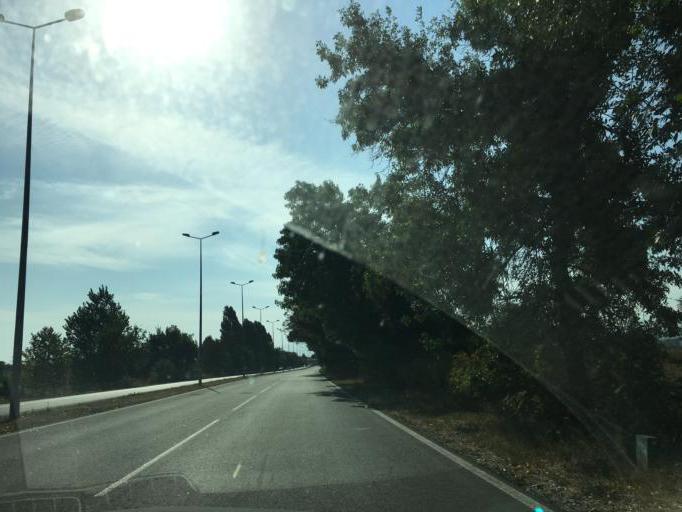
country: BG
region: Pazardzhik
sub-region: Obshtina Pazardzhik
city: Pazardzhik
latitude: 42.2173
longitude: 24.3167
